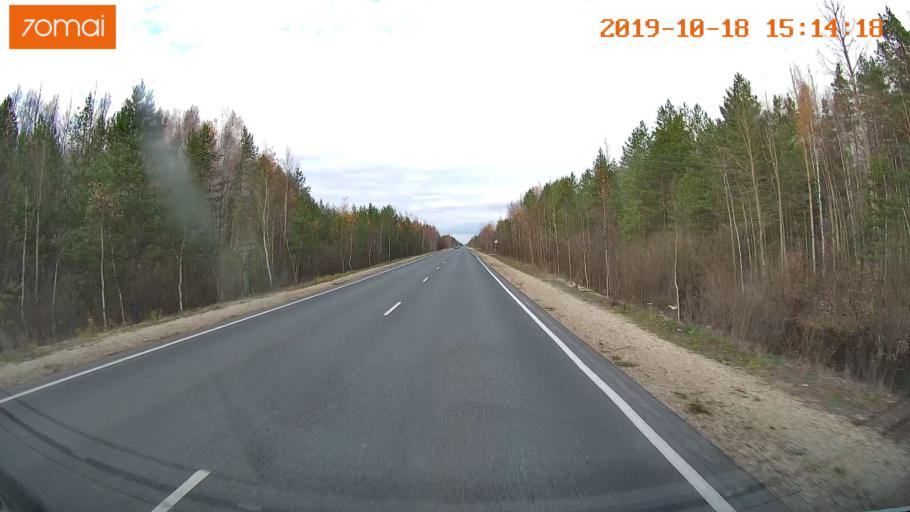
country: RU
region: Vladimir
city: Gus'-Khrustal'nyy
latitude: 55.6005
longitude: 40.7200
